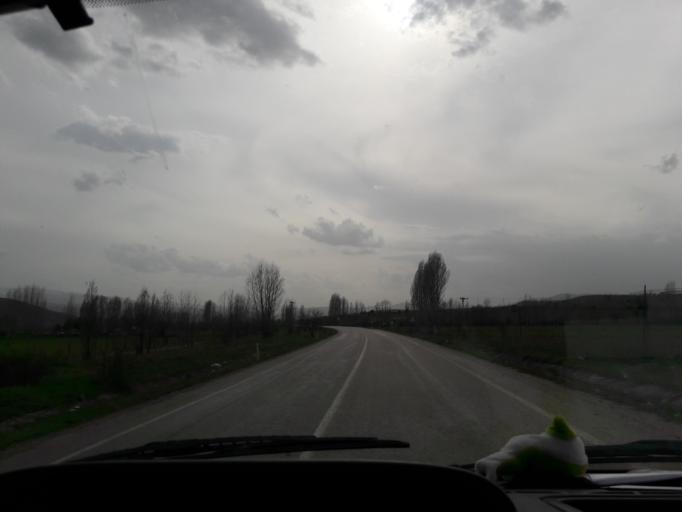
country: TR
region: Gumushane
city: Siran
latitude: 40.1772
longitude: 39.0940
